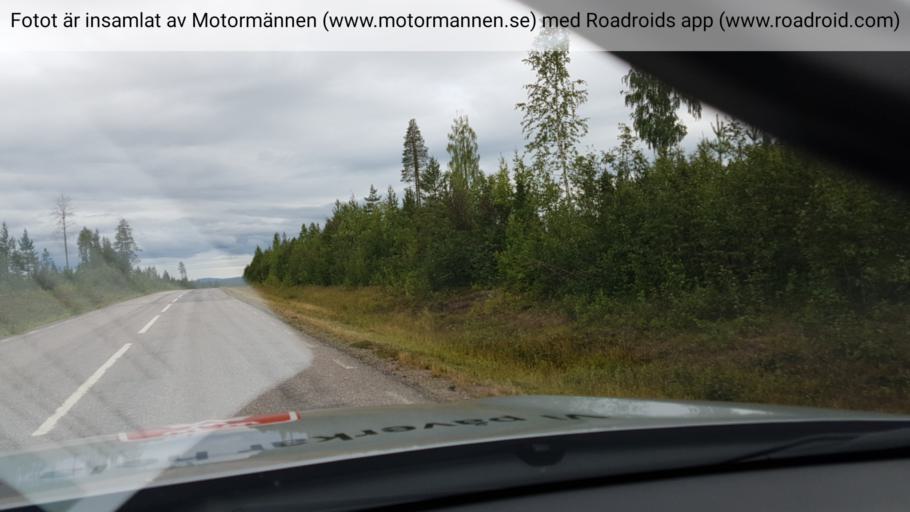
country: SE
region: Norrbotten
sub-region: Pajala Kommun
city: Pajala
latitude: 66.8230
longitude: 23.0214
